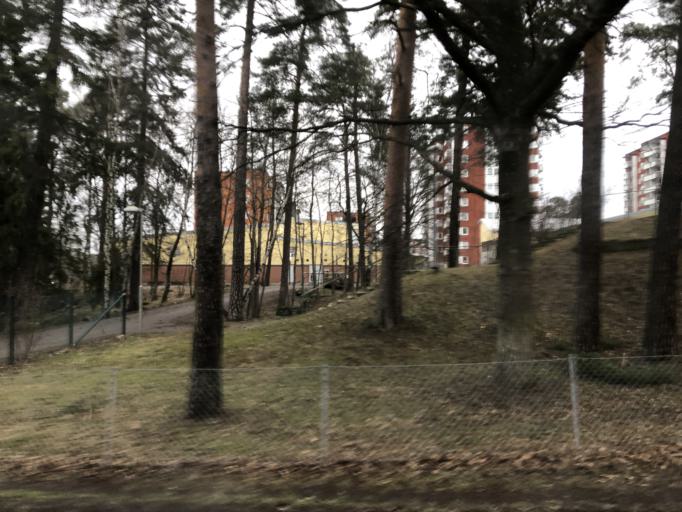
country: SE
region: Stockholm
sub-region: Stockholms Kommun
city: Kista
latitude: 59.4157
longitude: 17.9080
